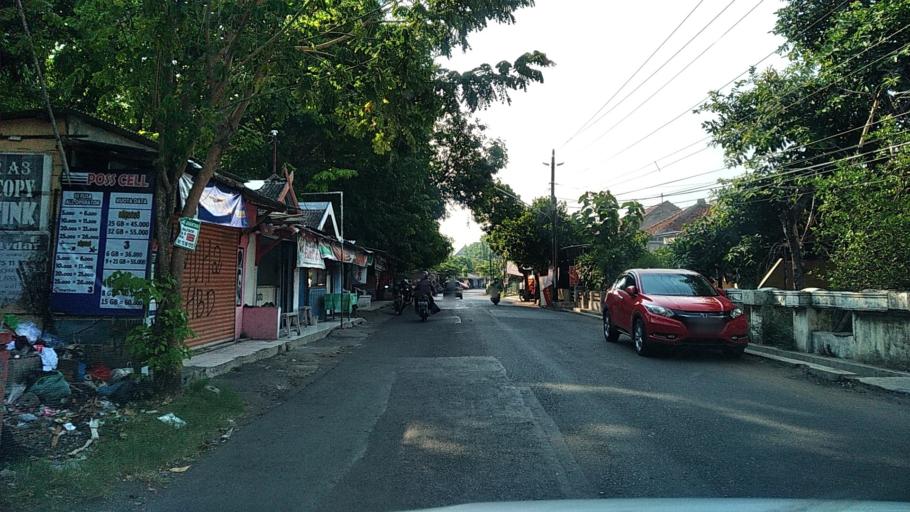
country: ID
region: Central Java
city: Semarang
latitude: -6.9955
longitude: 110.4275
